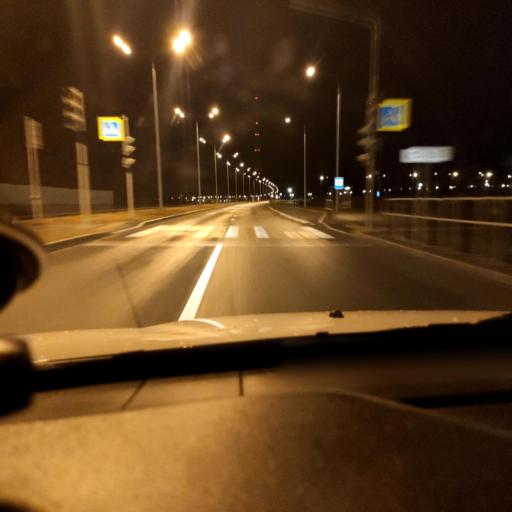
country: RU
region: Samara
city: Samara
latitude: 53.2851
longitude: 50.2360
